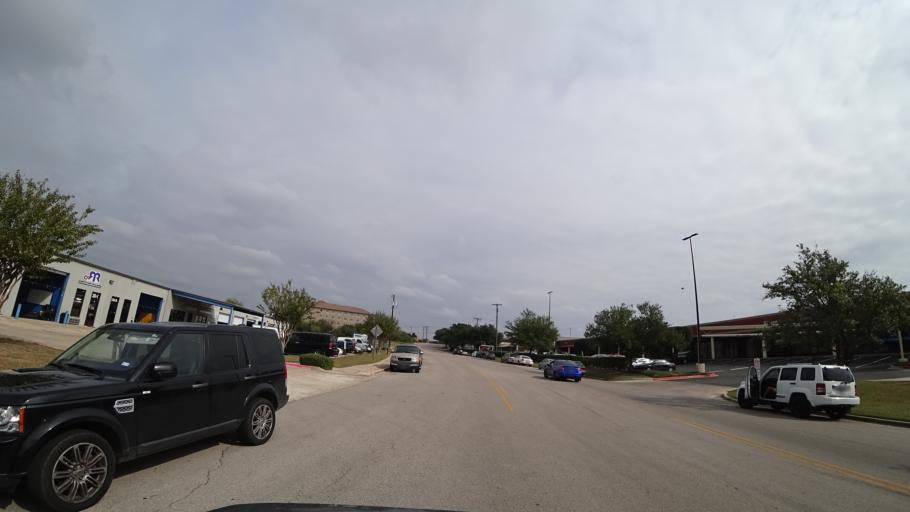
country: US
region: Texas
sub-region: Williamson County
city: Round Rock
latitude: 30.4908
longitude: -97.6809
